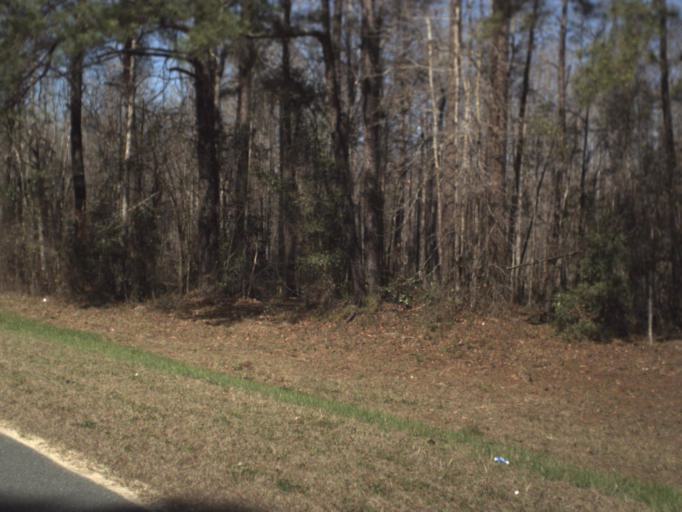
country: US
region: Florida
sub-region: Jackson County
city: Marianna
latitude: 30.7405
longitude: -85.1248
